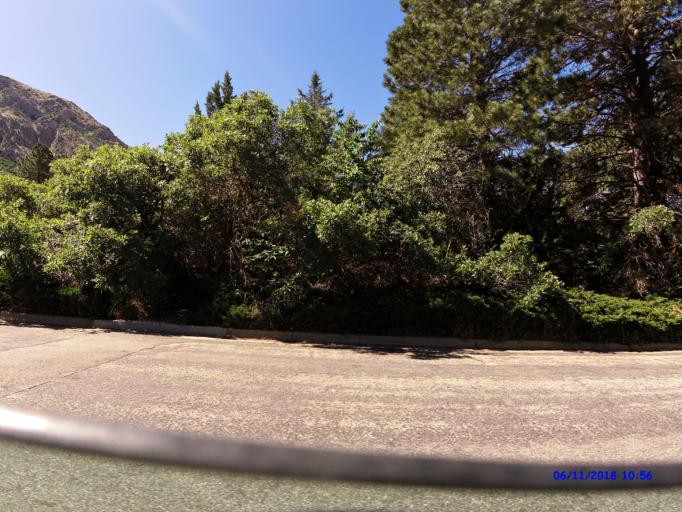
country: US
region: Utah
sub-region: Weber County
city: Ogden
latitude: 41.2159
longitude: -111.9304
